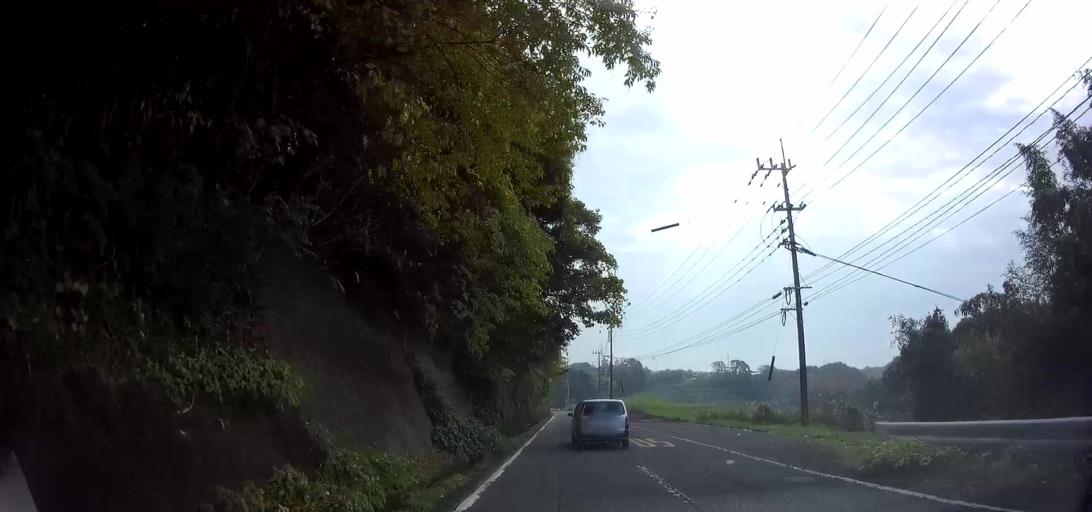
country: JP
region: Nagasaki
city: Shimabara
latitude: 32.6870
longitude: 130.2884
